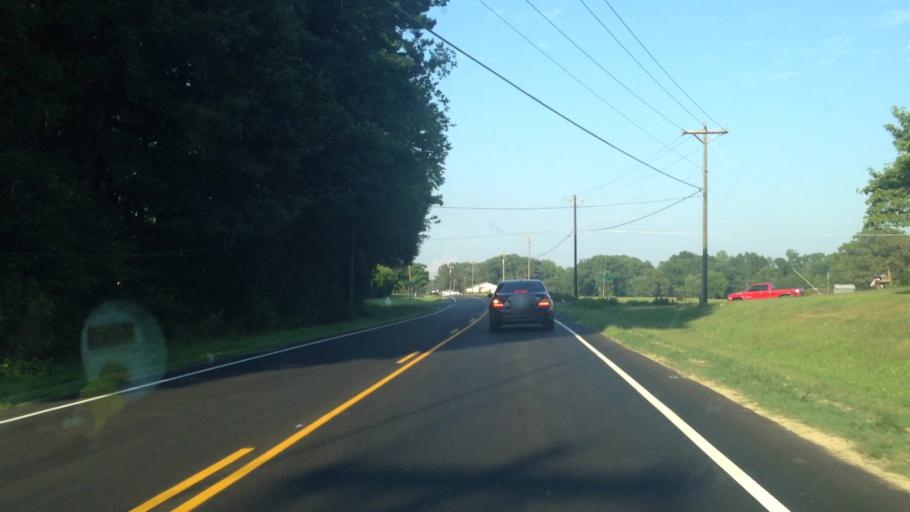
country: US
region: North Carolina
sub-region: Guilford County
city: Summerfield
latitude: 36.2510
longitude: -79.9026
